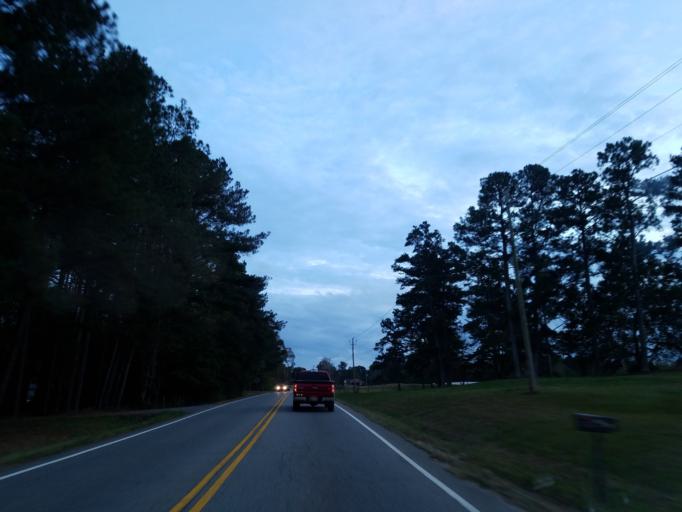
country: US
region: Georgia
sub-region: Dawson County
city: Dawsonville
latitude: 34.3405
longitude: -84.1189
